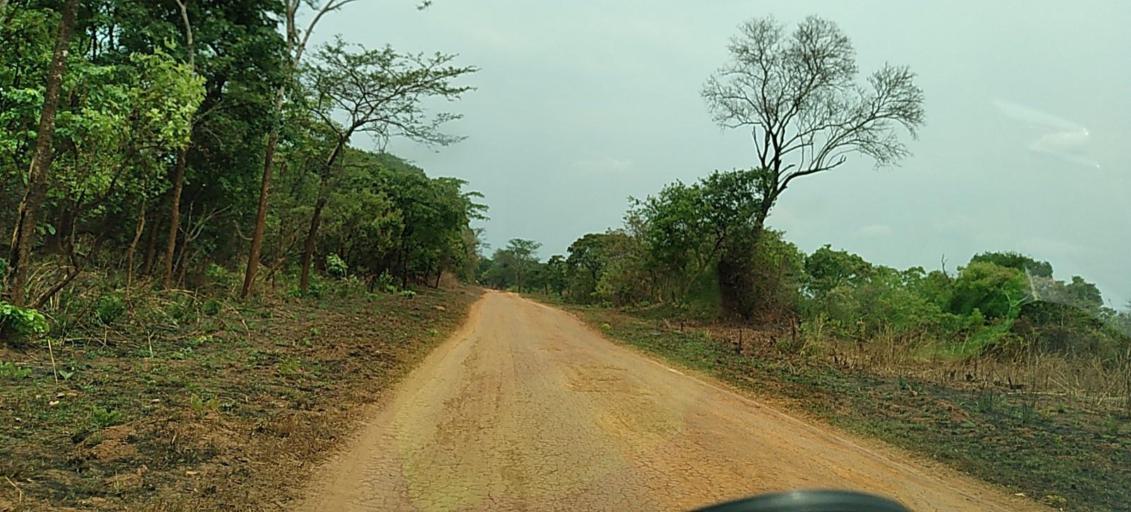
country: ZM
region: North-Western
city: Solwezi
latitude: -12.7984
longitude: 26.5341
